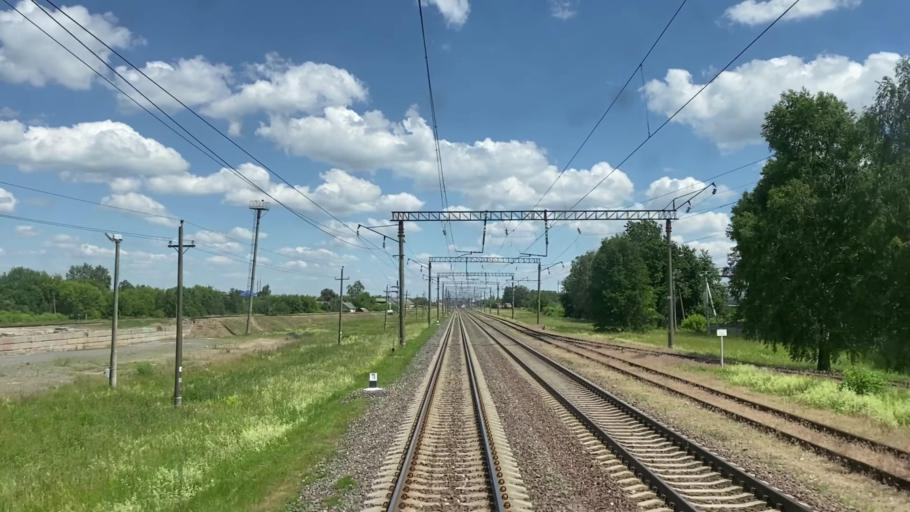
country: BY
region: Brest
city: Ivatsevichy
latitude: 52.6996
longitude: 25.3236
